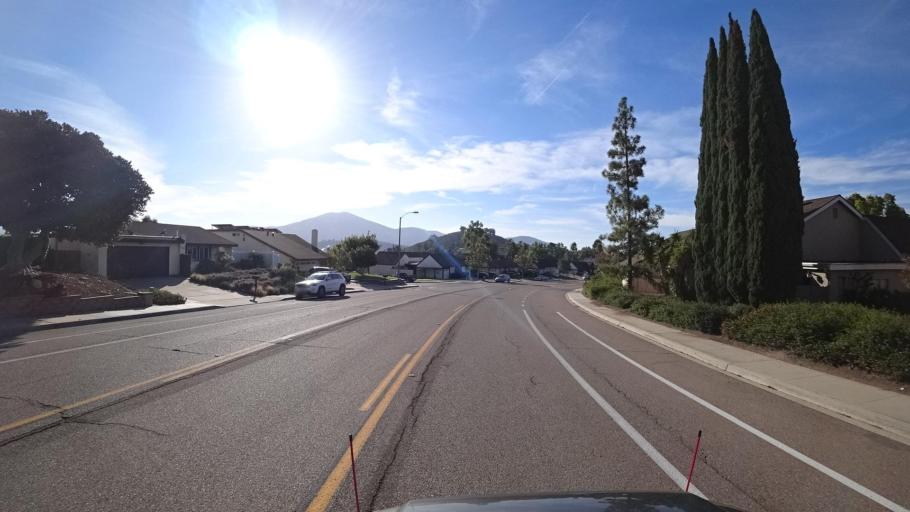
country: US
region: California
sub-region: San Diego County
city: Spring Valley
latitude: 32.7332
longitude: -116.9825
